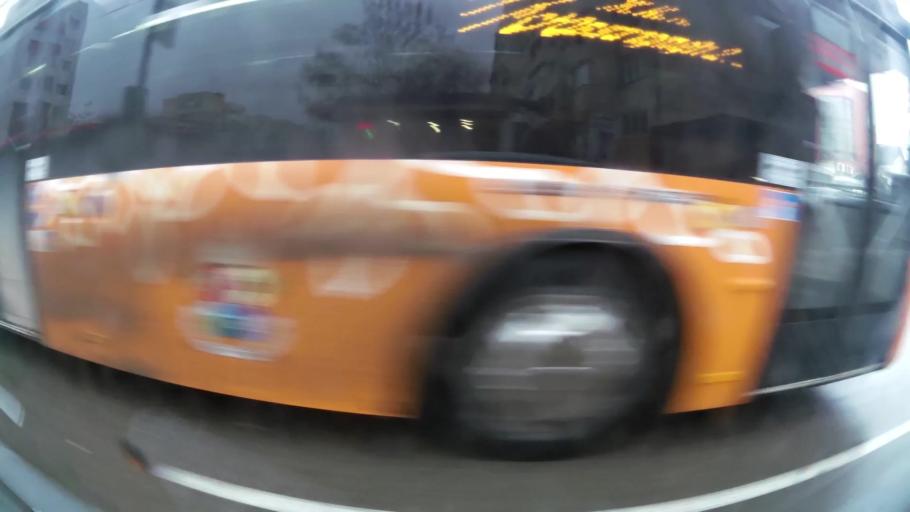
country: BG
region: Sofia-Capital
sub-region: Stolichna Obshtina
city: Sofia
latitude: 42.6900
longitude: 23.2546
